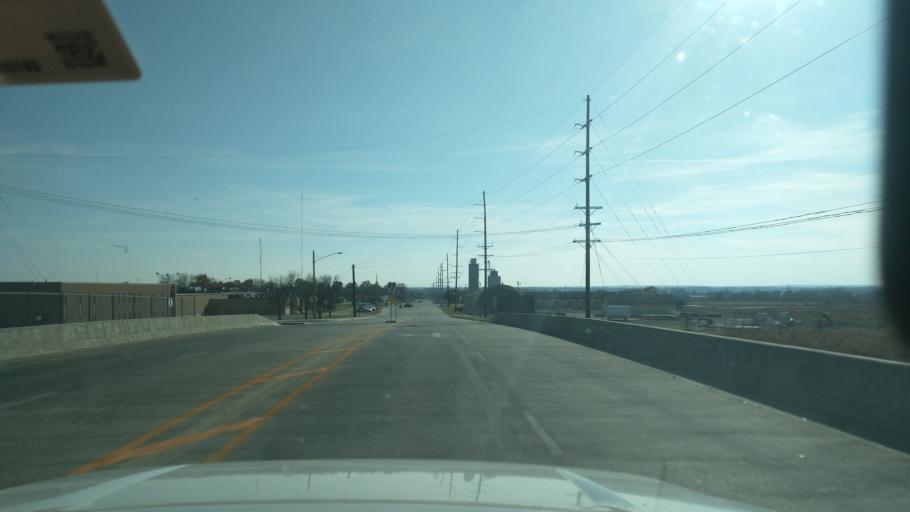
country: US
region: Kansas
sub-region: Lyon County
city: Emporia
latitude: 38.4156
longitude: -96.2263
